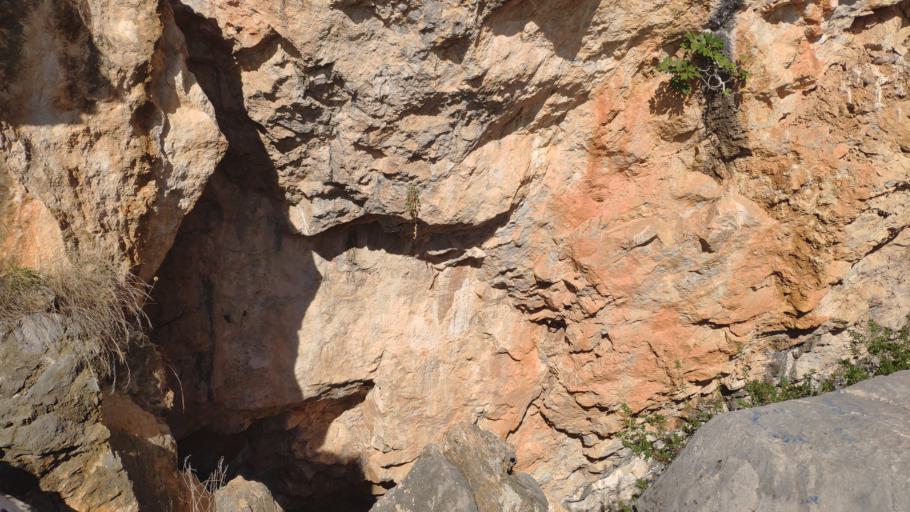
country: GR
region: Attica
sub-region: Nomos Piraios
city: Galatas
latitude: 37.5735
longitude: 23.3600
